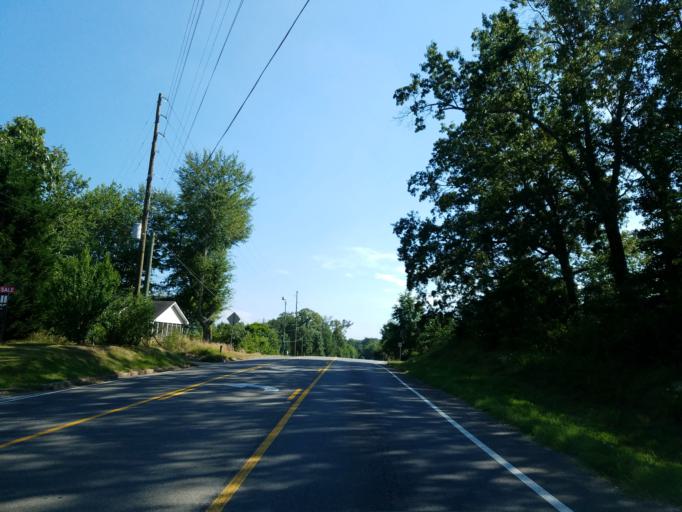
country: US
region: Georgia
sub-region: Fulton County
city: Milton
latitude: 34.2381
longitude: -84.2890
